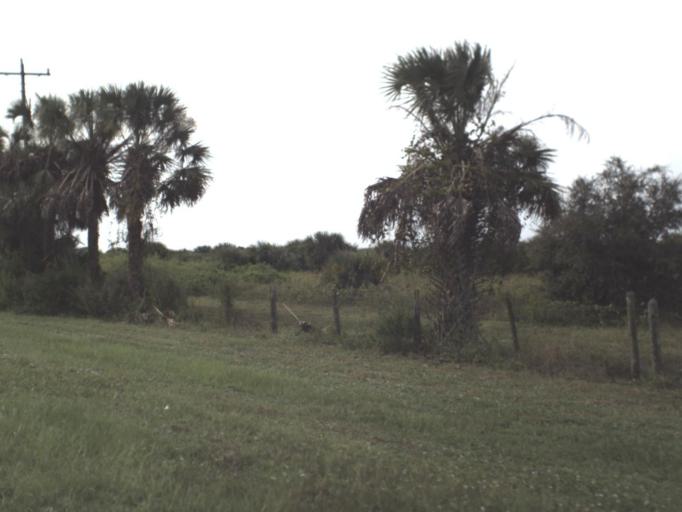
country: US
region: Florida
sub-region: Hendry County
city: Port LaBelle
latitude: 26.7685
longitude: -81.2846
